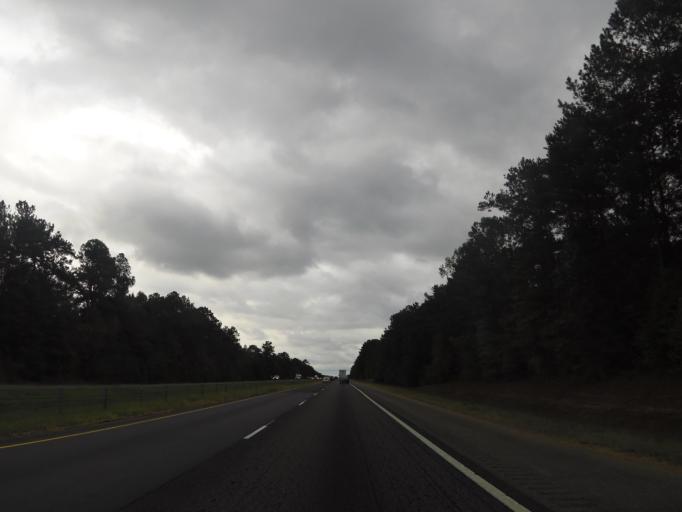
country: US
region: Alabama
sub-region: Butler County
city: Georgiana
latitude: 31.6166
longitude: -86.8096
